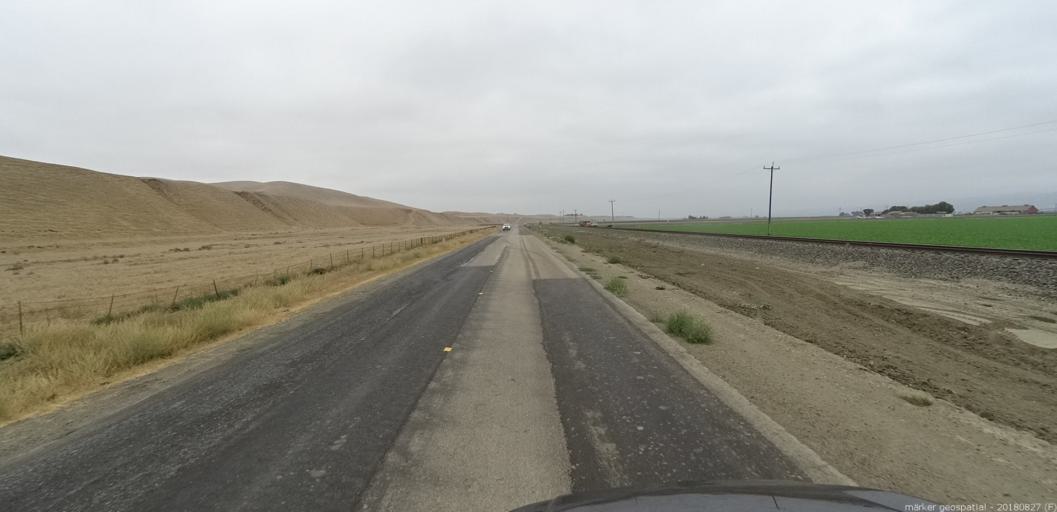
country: US
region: California
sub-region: Monterey County
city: Greenfield
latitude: 36.3040
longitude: -121.1625
